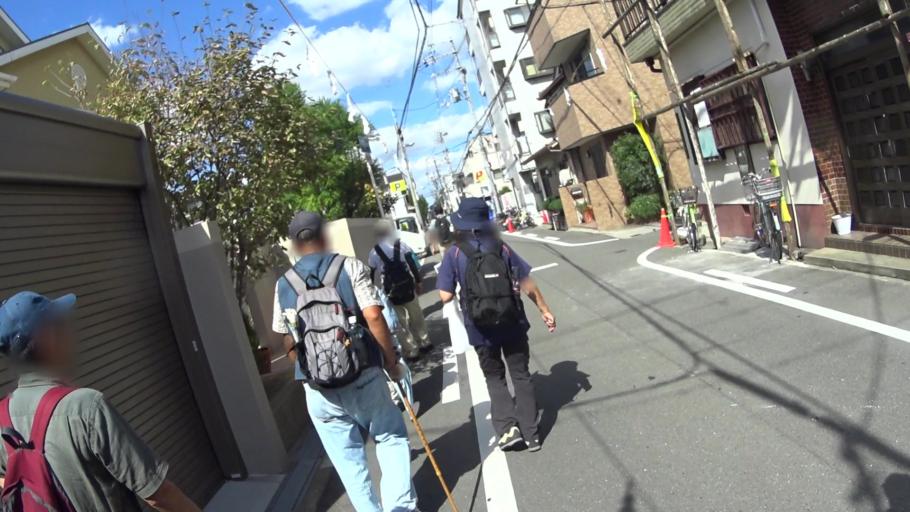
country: JP
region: Osaka
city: Yao
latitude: 34.6443
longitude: 135.5523
